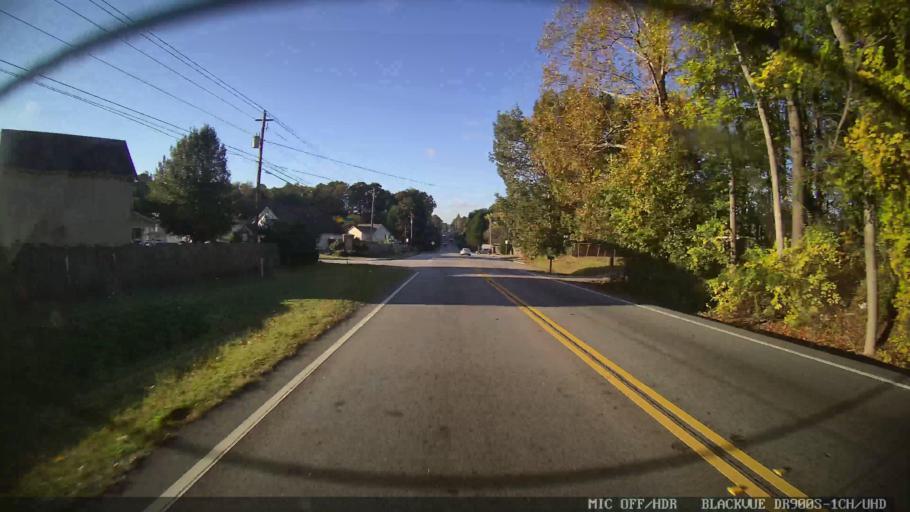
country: US
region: Georgia
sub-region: Clayton County
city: Lake City
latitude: 33.5974
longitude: -84.2969
